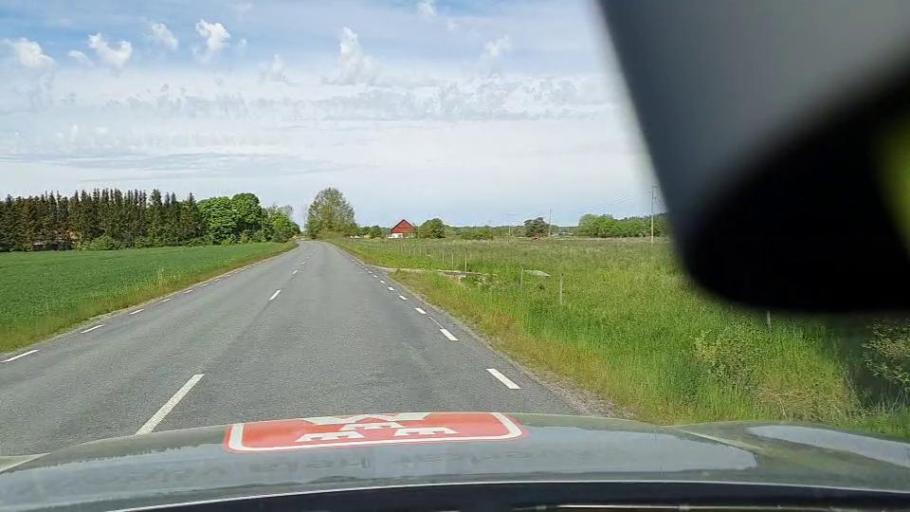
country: SE
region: Soedermanland
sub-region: Eskilstuna Kommun
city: Skogstorp
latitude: 59.3051
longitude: 16.4625
